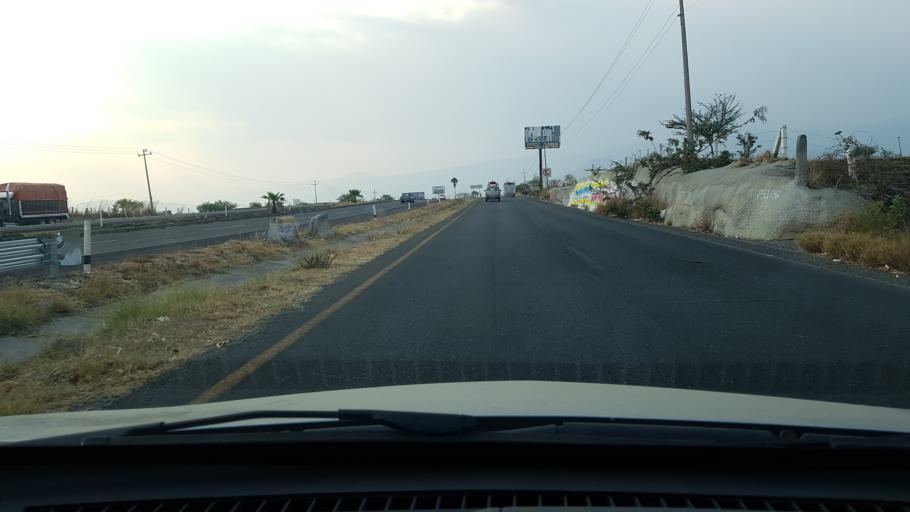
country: MX
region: Morelos
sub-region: Cuautla
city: Tierra Larga (Campo Nuevo)
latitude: 18.8688
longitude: -98.9529
